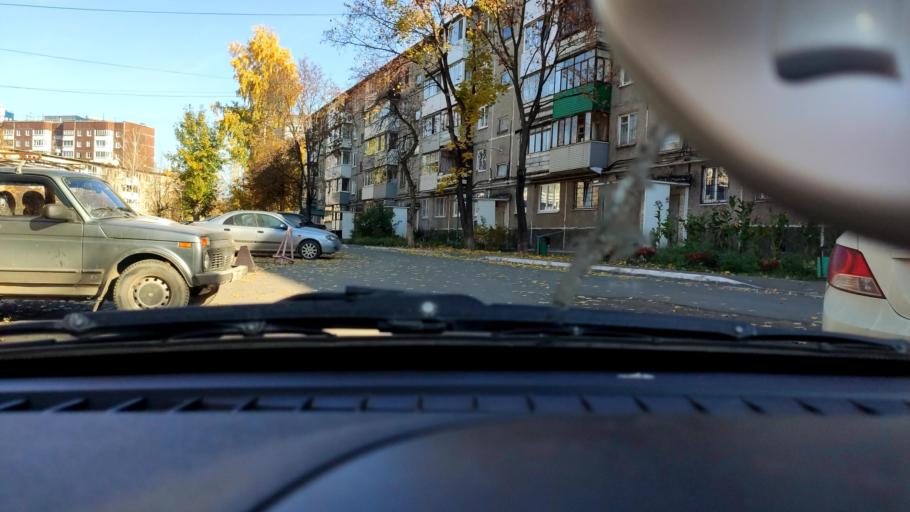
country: RU
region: Perm
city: Kondratovo
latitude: 57.9653
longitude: 56.1669
